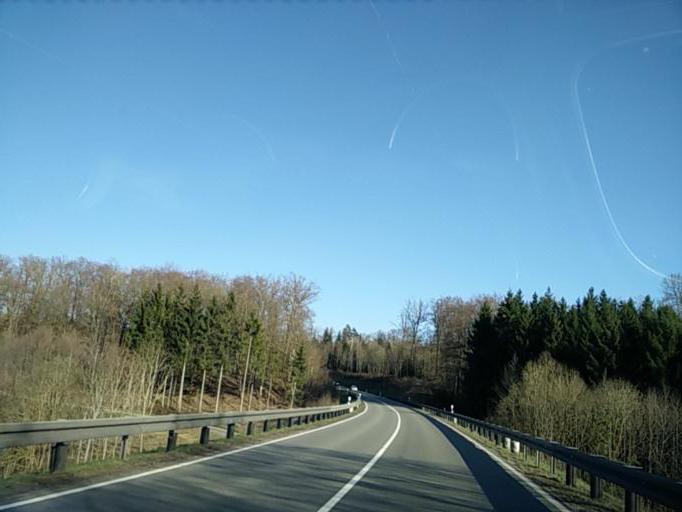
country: DE
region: Baden-Wuerttemberg
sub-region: Regierungsbezirk Stuttgart
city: Holzgerlingen
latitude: 48.6125
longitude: 9.0272
